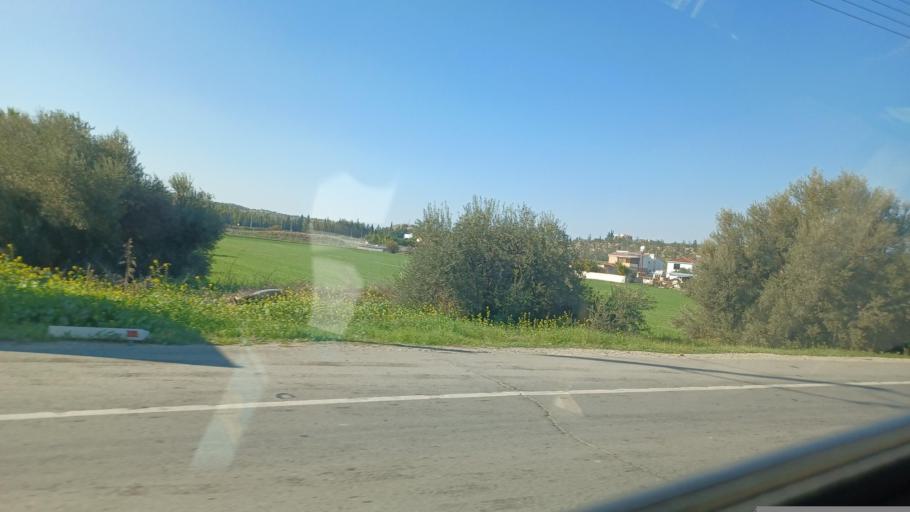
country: CY
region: Lefkosia
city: Alampra
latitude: 35.0050
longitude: 33.3939
